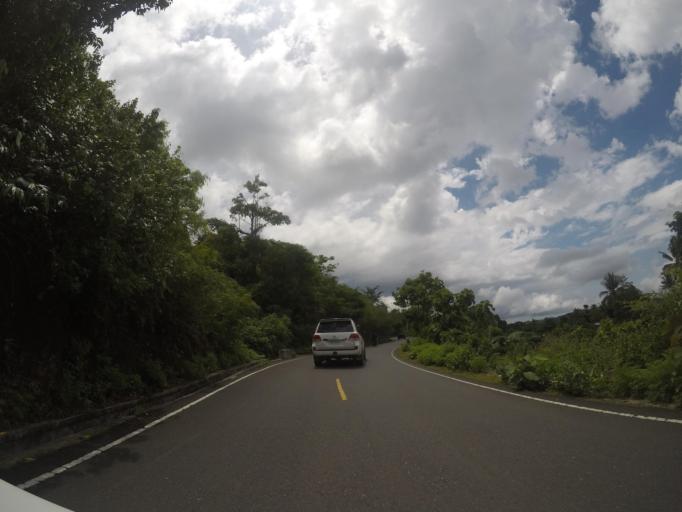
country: TL
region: Bobonaro
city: Maliana
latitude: -8.9591
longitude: 125.0591
